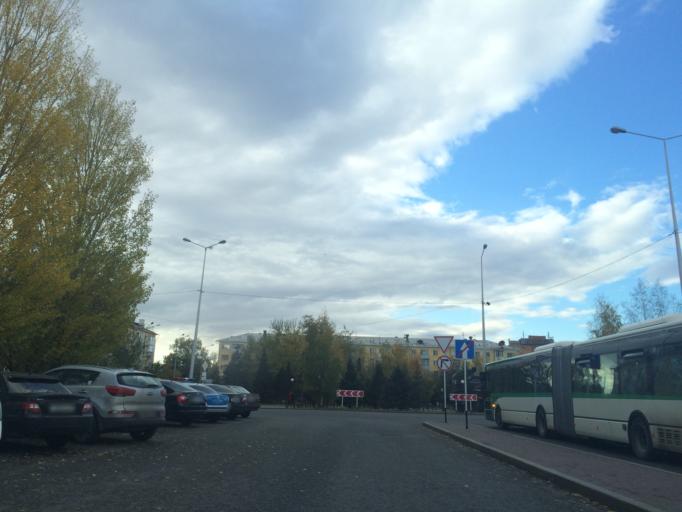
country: KZ
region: Astana Qalasy
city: Astana
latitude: 51.1948
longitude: 71.4084
